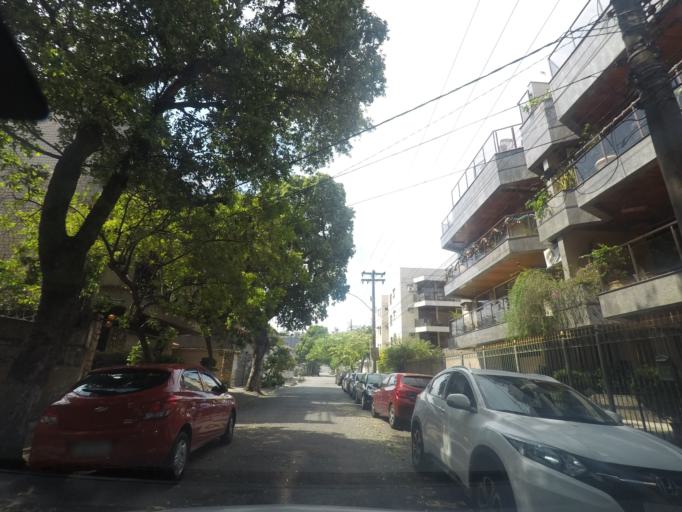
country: BR
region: Rio de Janeiro
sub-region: Rio De Janeiro
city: Rio de Janeiro
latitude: -22.8184
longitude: -43.2005
